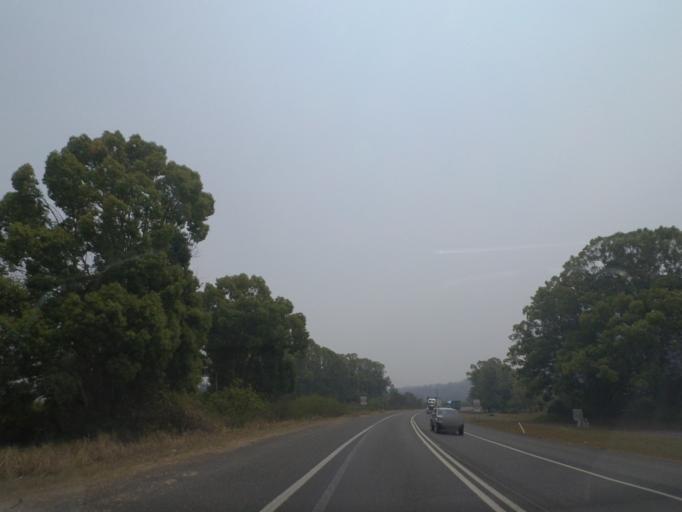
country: AU
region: New South Wales
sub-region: Clarence Valley
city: Maclean
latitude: -29.5462
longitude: 153.1558
